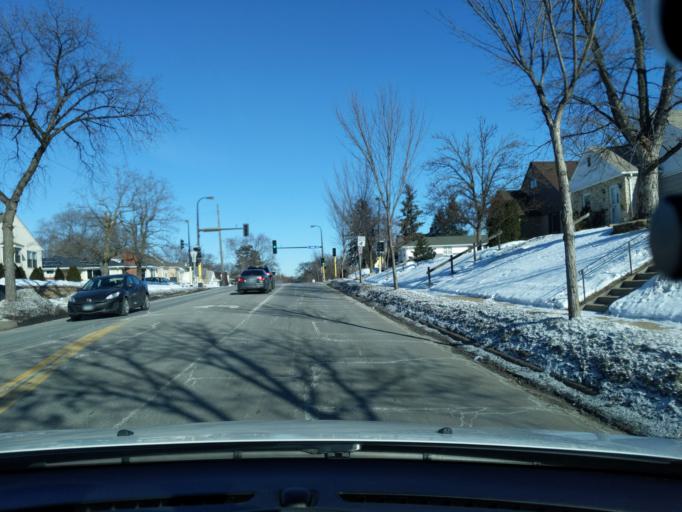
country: US
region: Minnesota
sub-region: Hennepin County
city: Richfield
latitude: 44.9191
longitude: -93.2473
